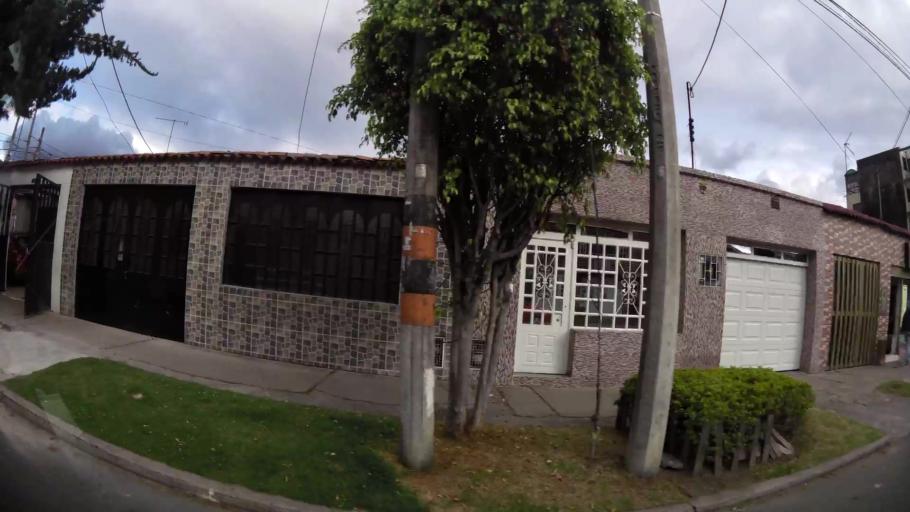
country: CO
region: Bogota D.C.
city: Bogota
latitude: 4.6068
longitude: -74.1146
